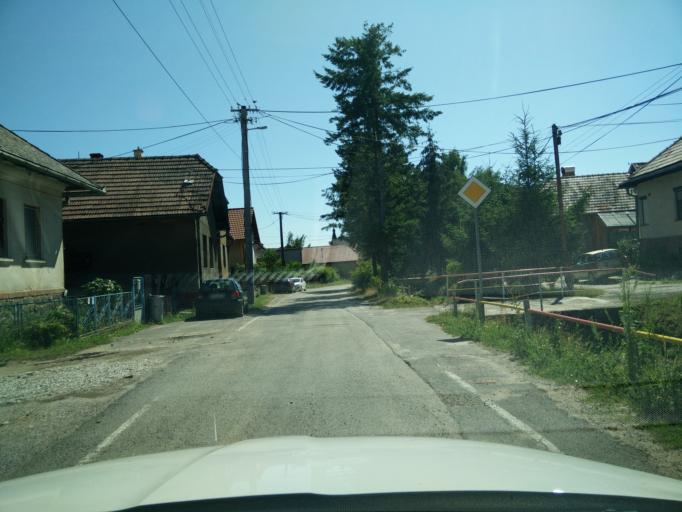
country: SK
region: Nitriansky
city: Prievidza
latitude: 48.8007
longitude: 18.7022
